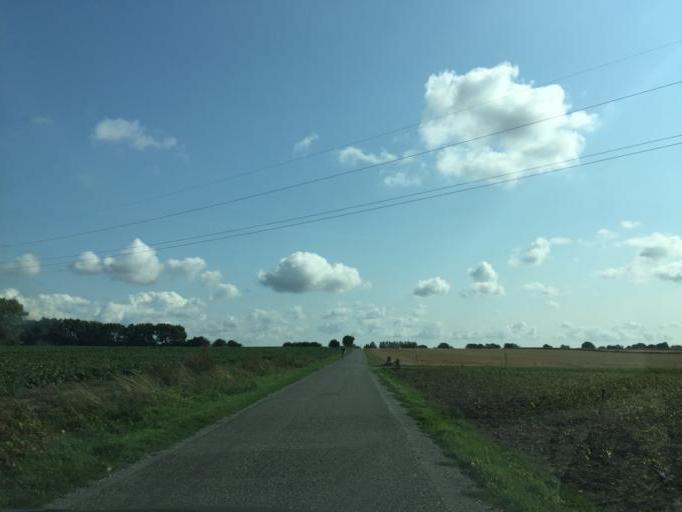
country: DK
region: South Denmark
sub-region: Odense Kommune
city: Bellinge
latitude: 55.3176
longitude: 10.3765
